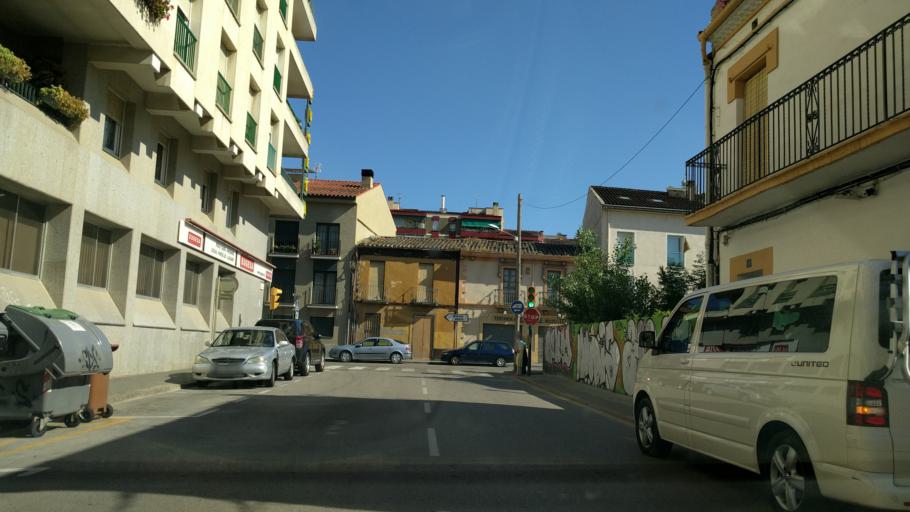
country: ES
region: Catalonia
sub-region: Provincia de Girona
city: Salt
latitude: 41.9753
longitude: 2.7897
